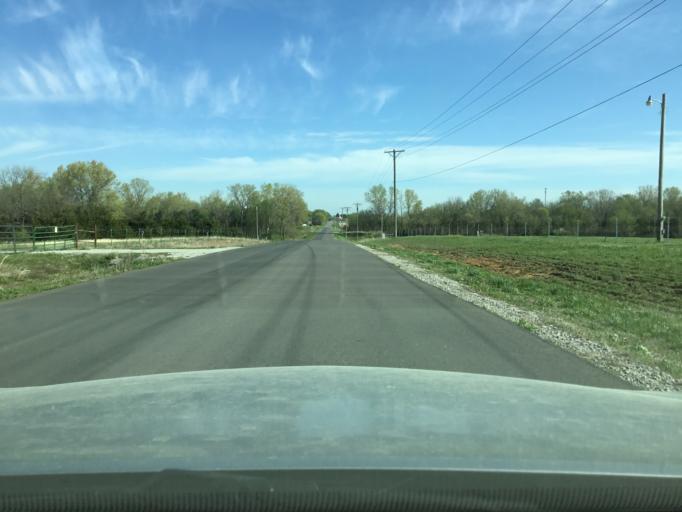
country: US
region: Kansas
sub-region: Neosho County
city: Chanute
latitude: 37.6550
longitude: -95.4435
